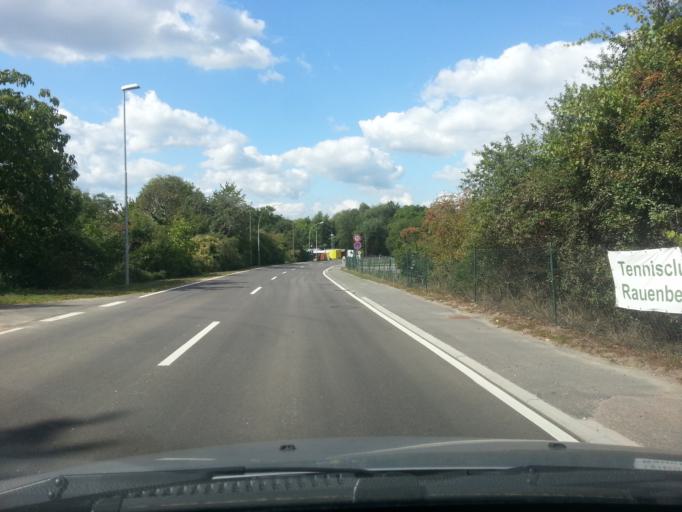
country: DE
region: Baden-Wuerttemberg
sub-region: Karlsruhe Region
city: Malsch
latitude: 49.2584
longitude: 8.6742
